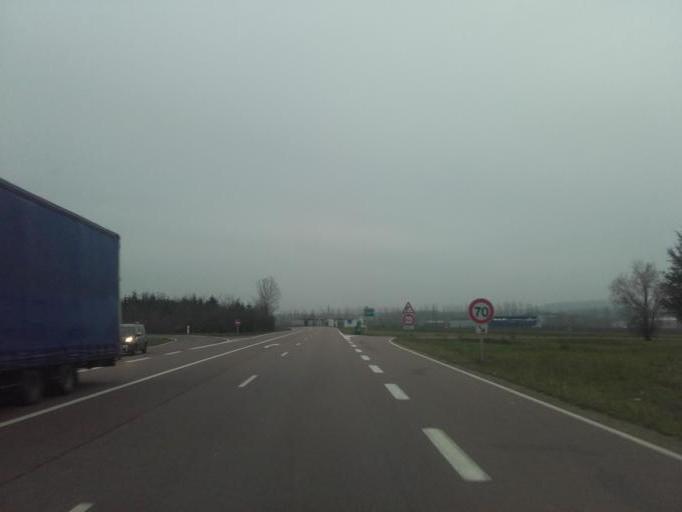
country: FR
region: Bourgogne
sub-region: Departement de la Cote-d'Or
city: Corpeau
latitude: 46.9270
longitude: 4.7428
